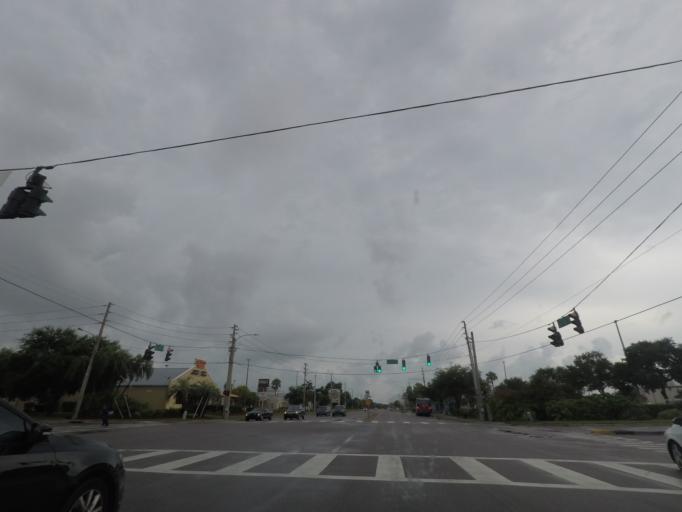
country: US
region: Florida
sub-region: Pinellas County
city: Kenneth City
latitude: 27.7918
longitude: -82.7335
